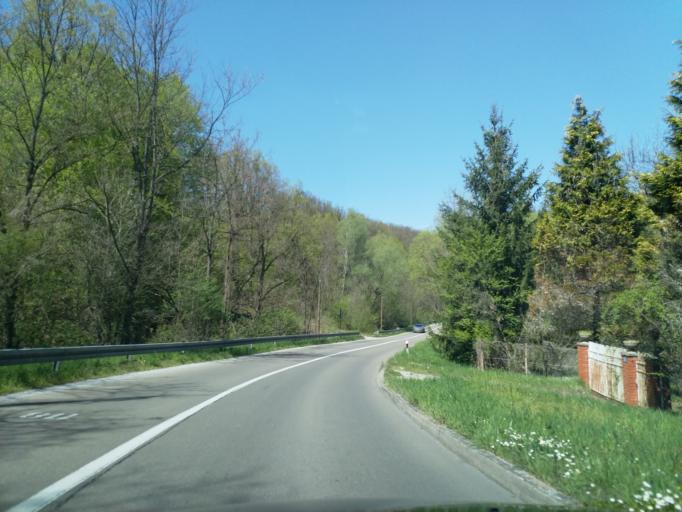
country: RS
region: Central Serbia
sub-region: Belgrade
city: Lazarevac
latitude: 44.3563
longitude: 20.3519
